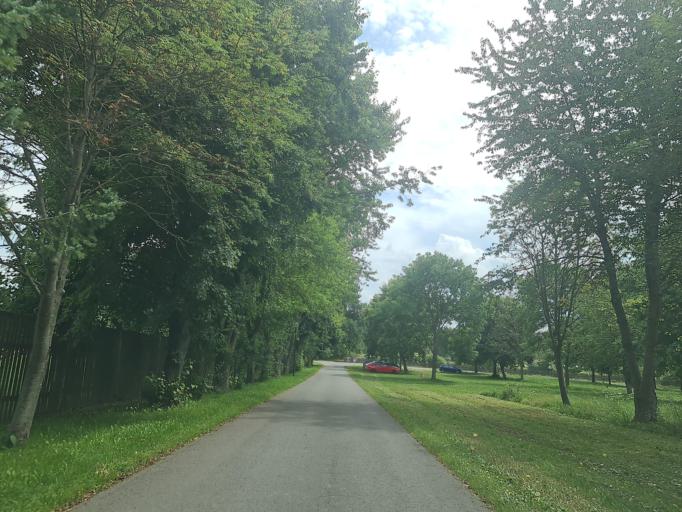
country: DE
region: Saxony
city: Hirschfeld
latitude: 50.6259
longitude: 12.4395
